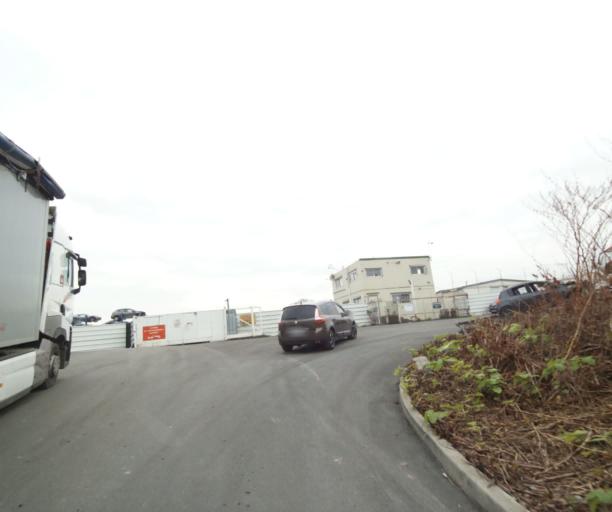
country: FR
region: Ile-de-France
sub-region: Departement de Seine-Saint-Denis
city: Le Blanc-Mesnil
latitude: 48.9630
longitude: 2.4645
